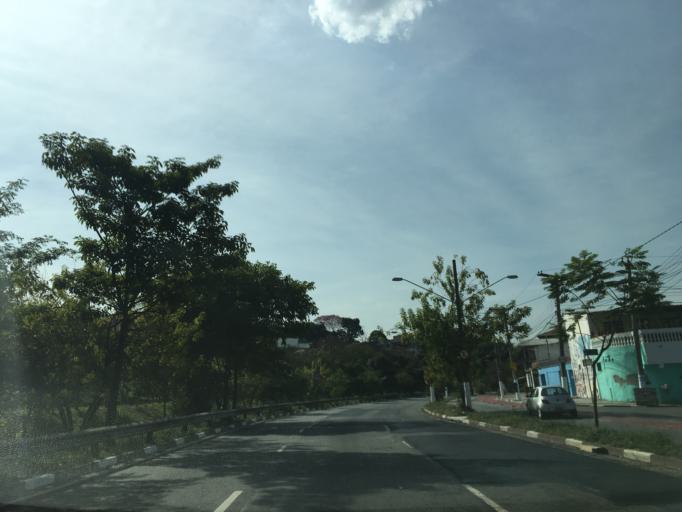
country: BR
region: Sao Paulo
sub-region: Osasco
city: Osasco
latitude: -23.5721
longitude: -46.7640
